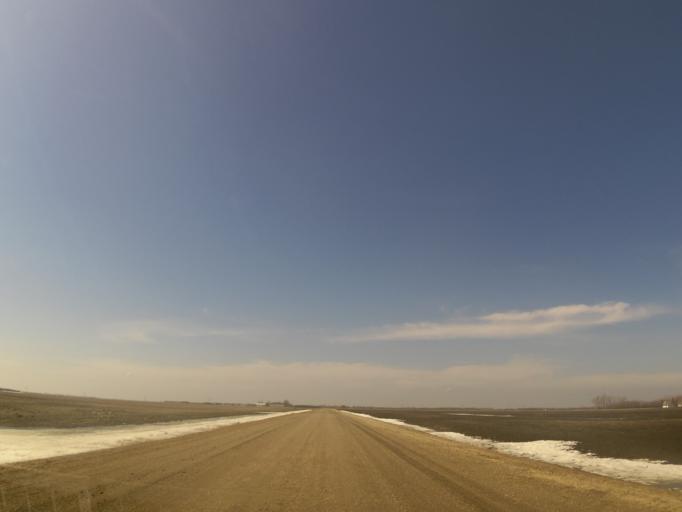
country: US
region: North Dakota
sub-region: Walsh County
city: Grafton
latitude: 48.4265
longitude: -97.2453
